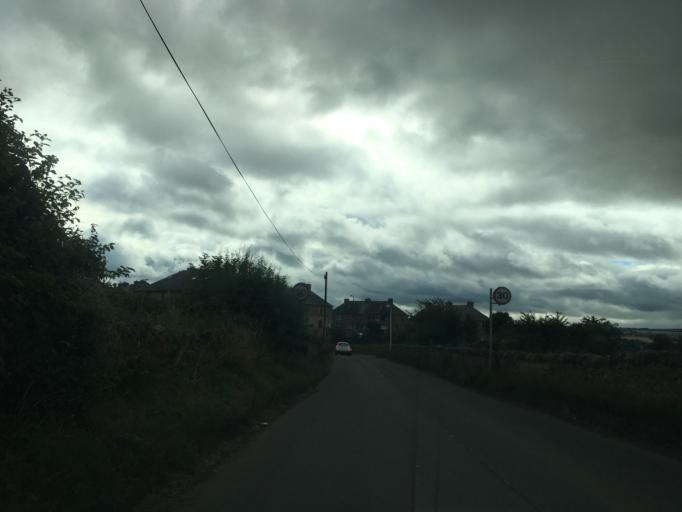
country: GB
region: Scotland
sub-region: Midlothian
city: Gorebridge
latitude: 55.8597
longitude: -3.0564
